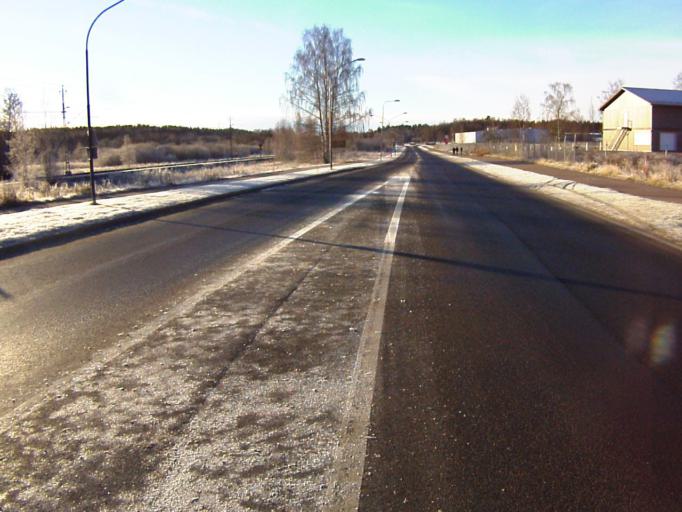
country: SE
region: Soedermanland
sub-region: Eskilstuna Kommun
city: Skogstorp
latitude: 59.3453
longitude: 16.4918
